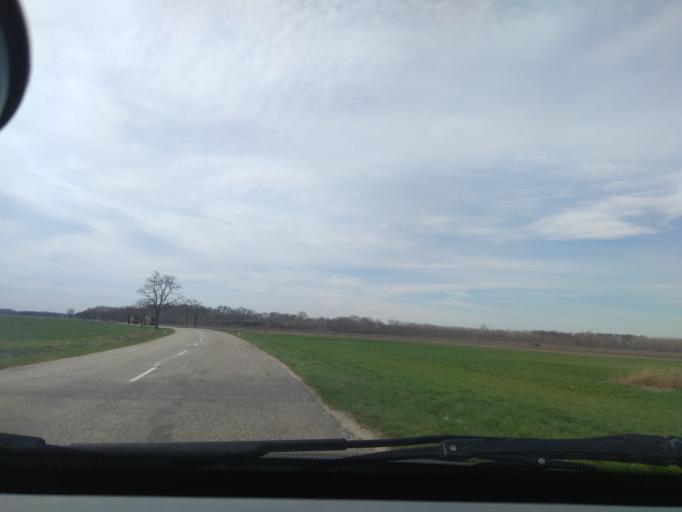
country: SK
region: Trnavsky
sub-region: Okres Dunajska Streda
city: Velky Meder
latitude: 47.8266
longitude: 17.7499
